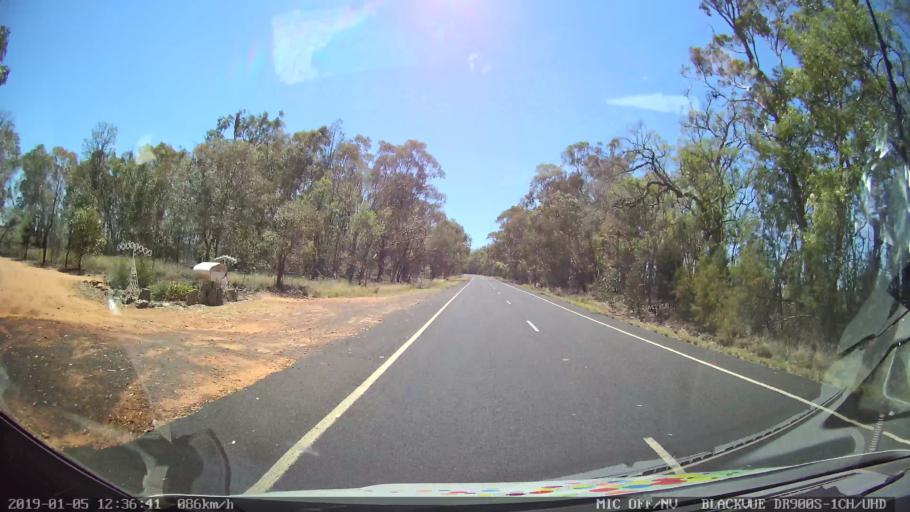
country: AU
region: New South Wales
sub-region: Warrumbungle Shire
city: Coonabarabran
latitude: -31.2065
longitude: 149.4441
